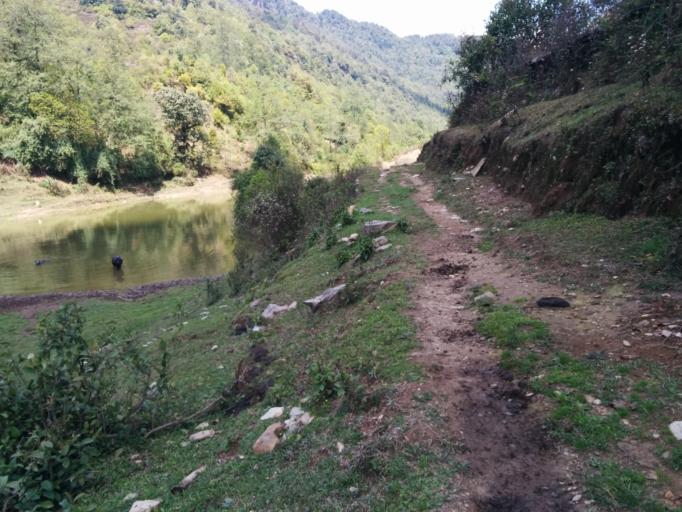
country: NP
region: Western Region
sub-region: Gandaki Zone
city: Pokhara
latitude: 28.2194
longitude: 83.8110
